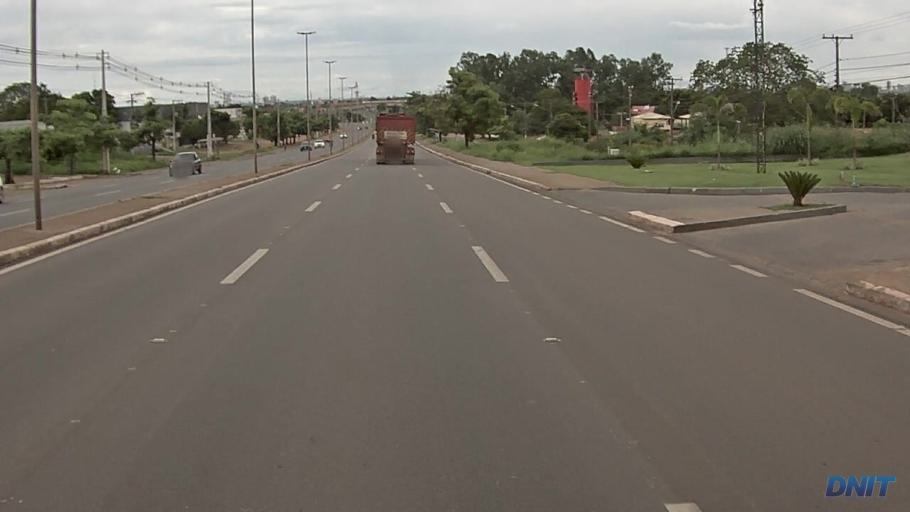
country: BR
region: Mato Grosso
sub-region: Cuiaba
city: Cuiaba
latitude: -15.6434
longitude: -56.0157
